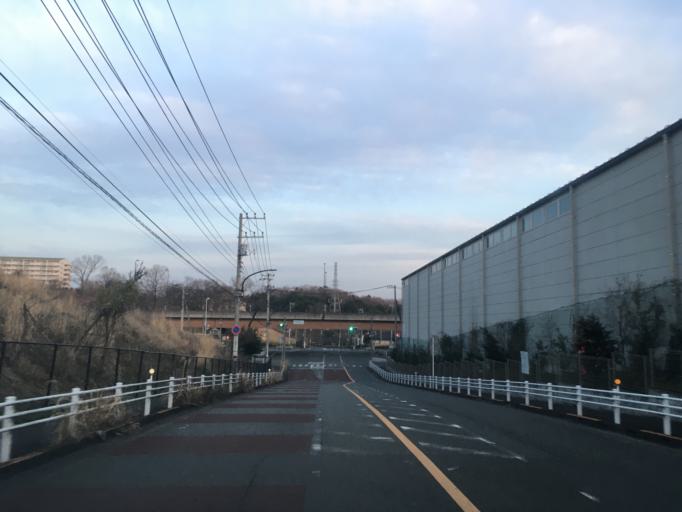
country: JP
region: Tokyo
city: Hino
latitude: 35.6024
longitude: 139.3875
